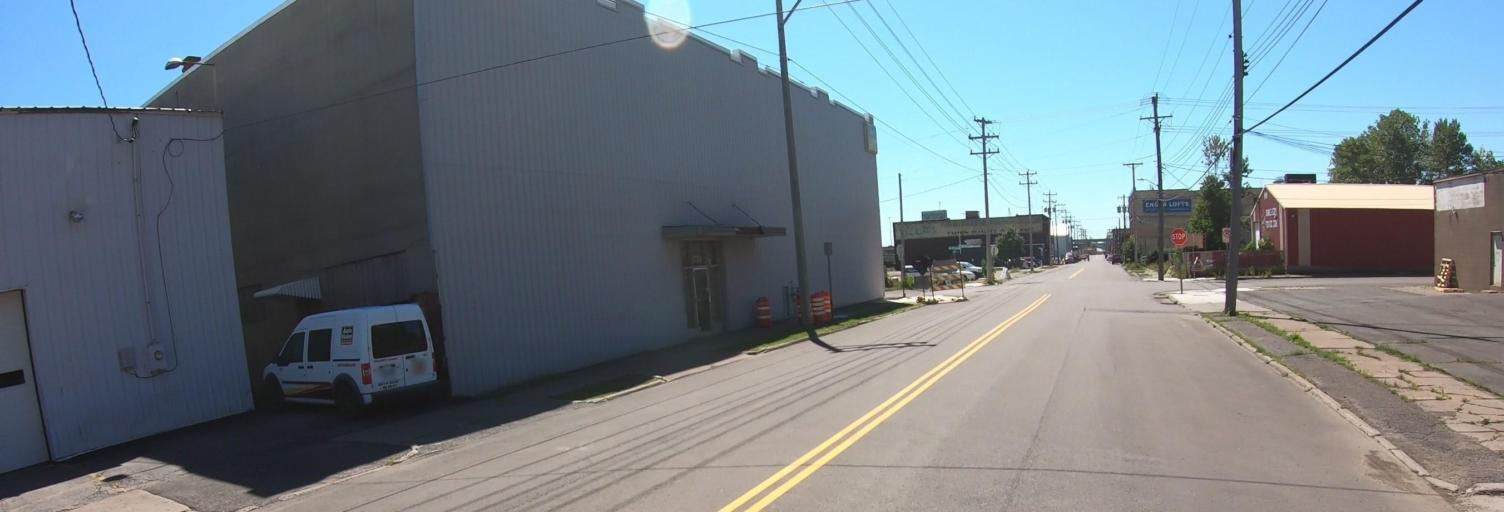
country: US
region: Minnesota
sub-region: Saint Louis County
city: Duluth
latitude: 46.7697
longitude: -92.1195
